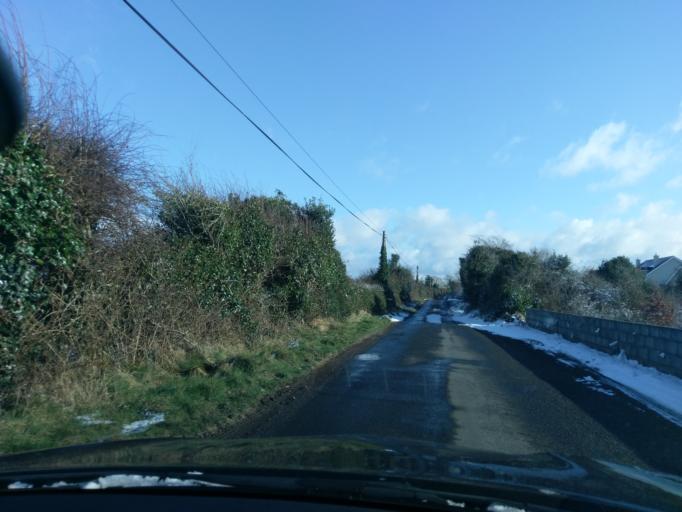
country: IE
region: Connaught
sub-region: County Galway
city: Athenry
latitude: 53.1902
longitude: -8.7900
